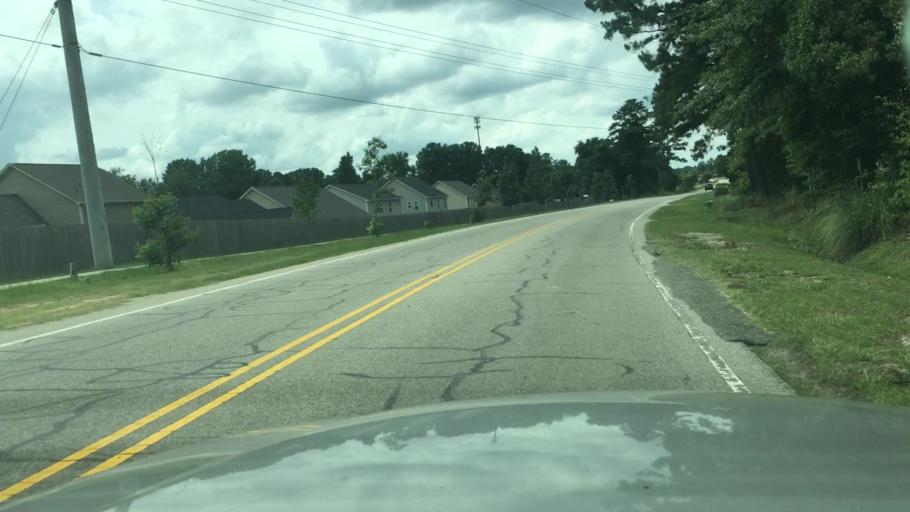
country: US
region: North Carolina
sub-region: Hoke County
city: Rockfish
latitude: 35.0089
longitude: -79.0017
